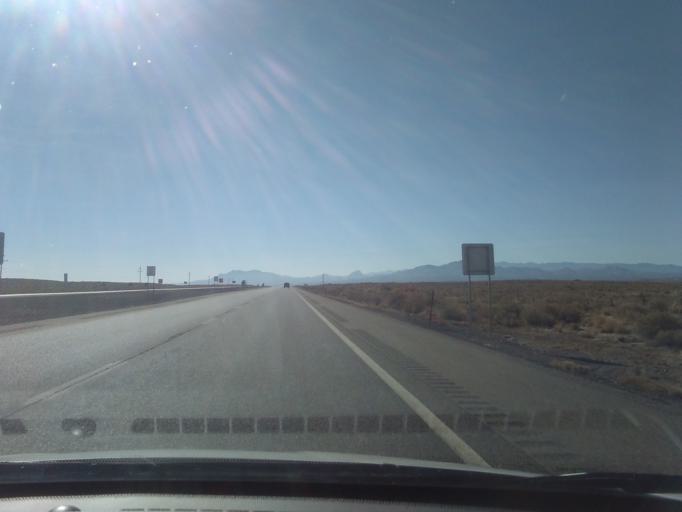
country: US
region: New Mexico
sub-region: Socorro County
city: Socorro
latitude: 34.3186
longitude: -106.8846
